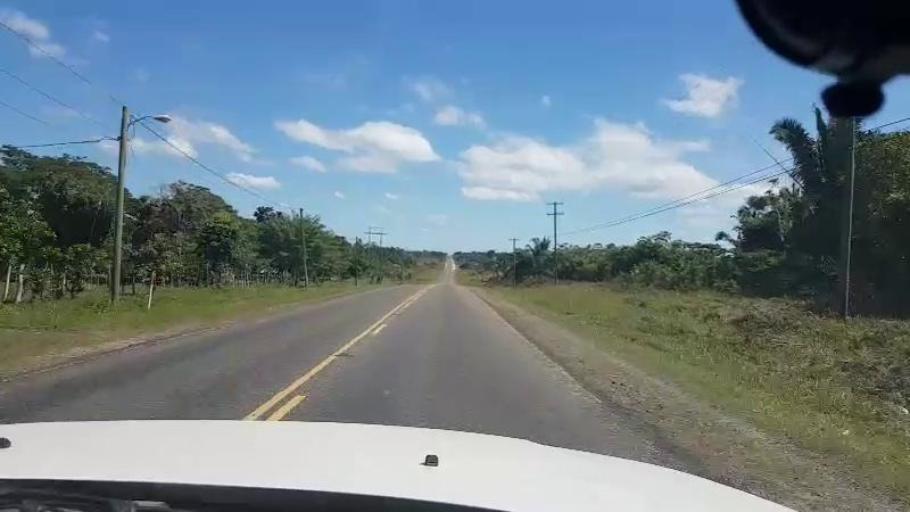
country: BZ
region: Cayo
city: Belmopan
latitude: 17.2768
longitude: -88.7274
